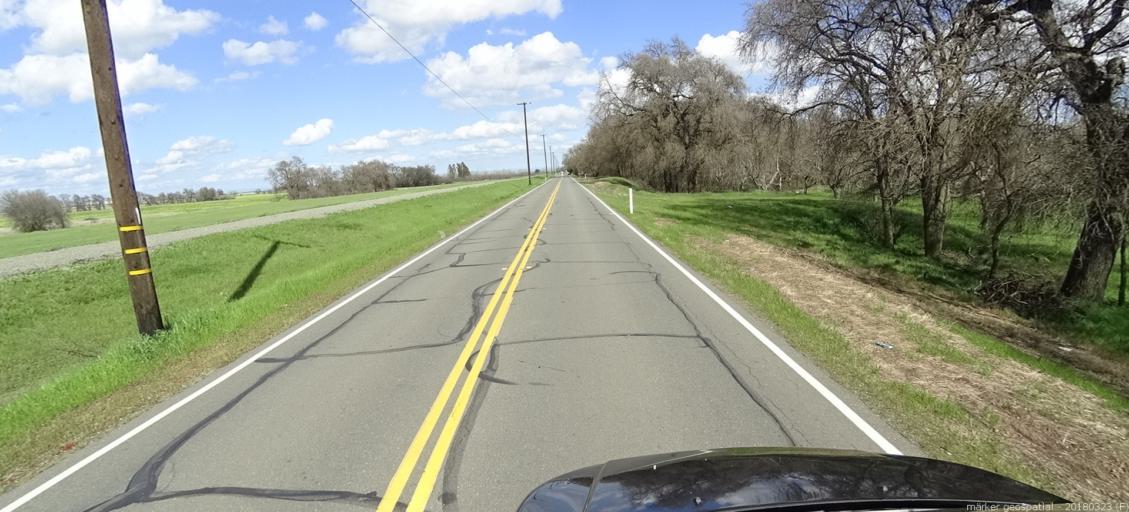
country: US
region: California
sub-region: Yolo County
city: West Sacramento
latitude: 38.6458
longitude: -121.5847
